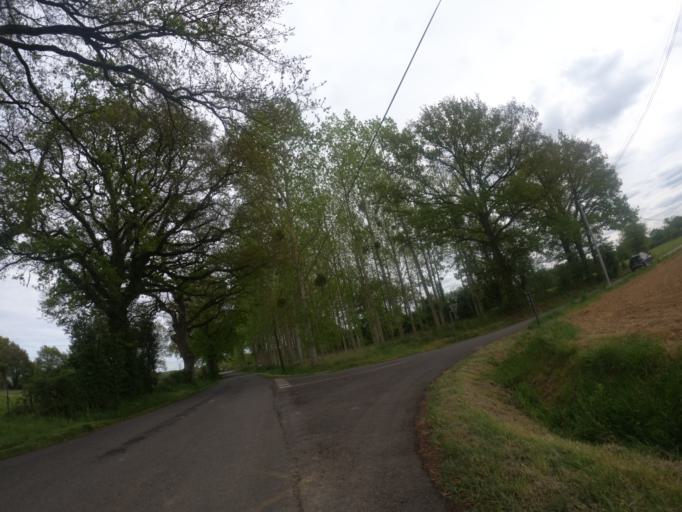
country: FR
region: Pays de la Loire
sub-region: Departement de la Loire-Atlantique
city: Rouge
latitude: 47.7378
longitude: -1.4310
